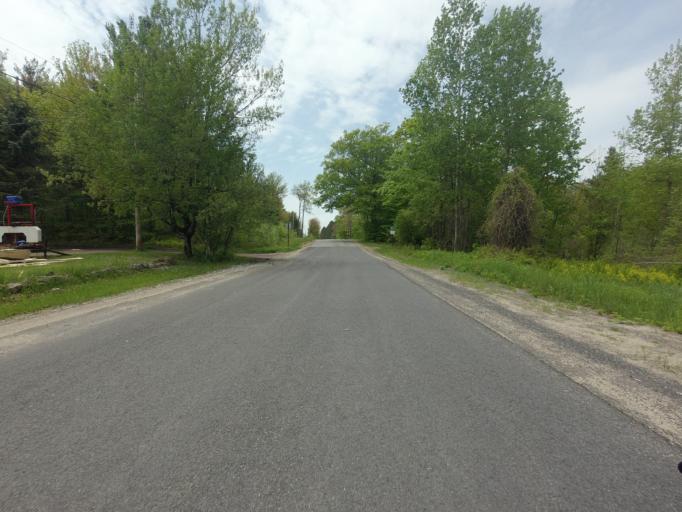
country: US
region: New York
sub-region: St. Lawrence County
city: Hannawa Falls
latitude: 44.5531
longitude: -74.9532
